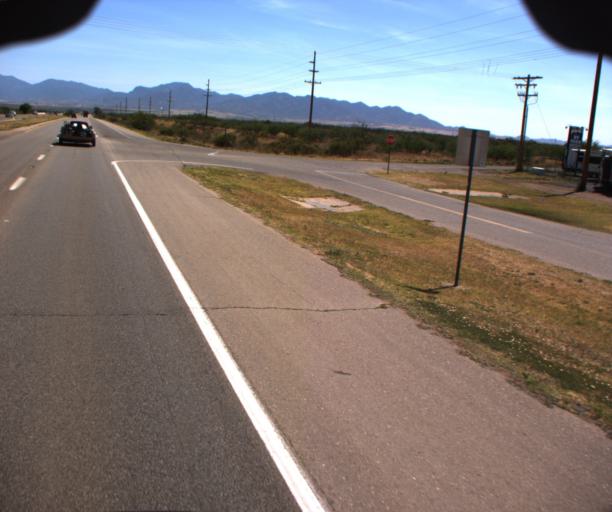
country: US
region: Arizona
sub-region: Cochise County
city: Huachuca City
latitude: 31.6835
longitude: -110.3504
